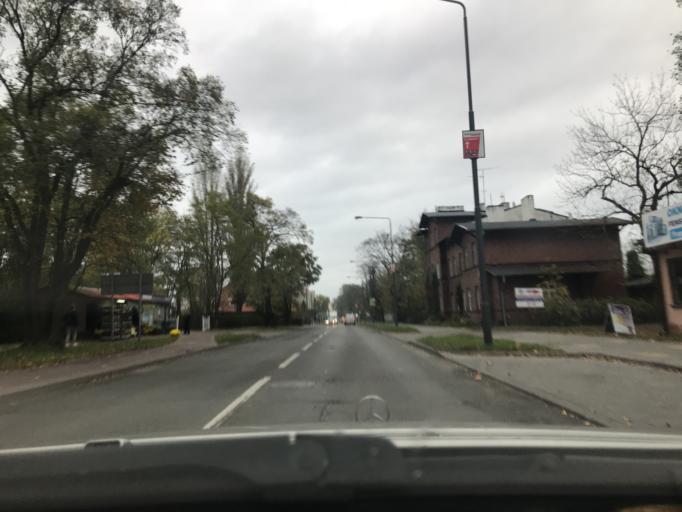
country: PL
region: West Pomeranian Voivodeship
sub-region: Swinoujscie
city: Swinoujscie
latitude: 53.9004
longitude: 14.2341
